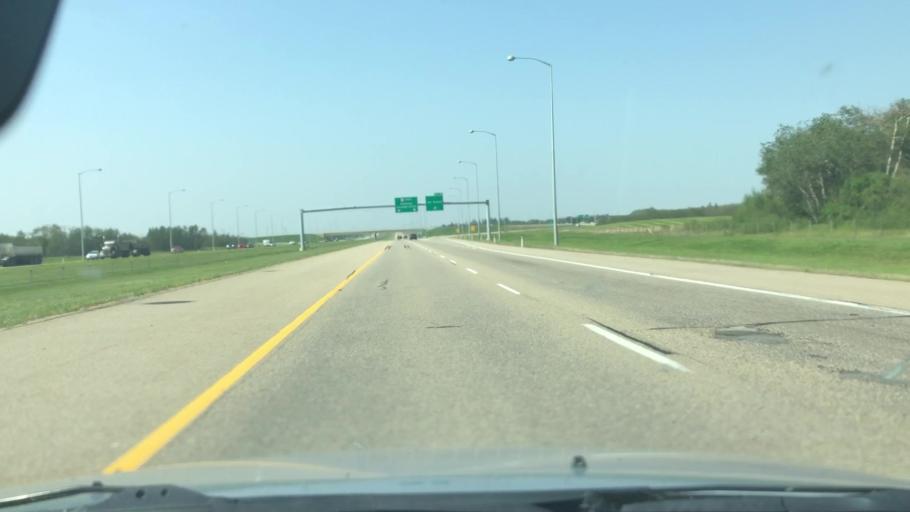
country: CA
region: Alberta
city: St. Albert
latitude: 53.6431
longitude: -113.5337
